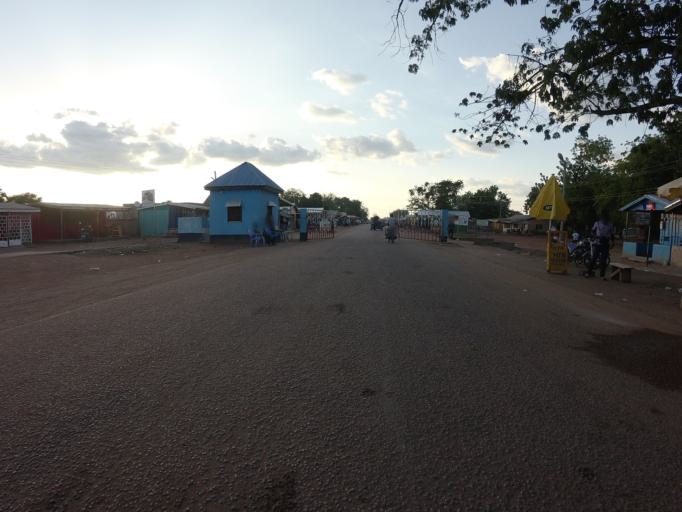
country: GH
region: Upper East
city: Navrongo
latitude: 10.9937
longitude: -1.1124
